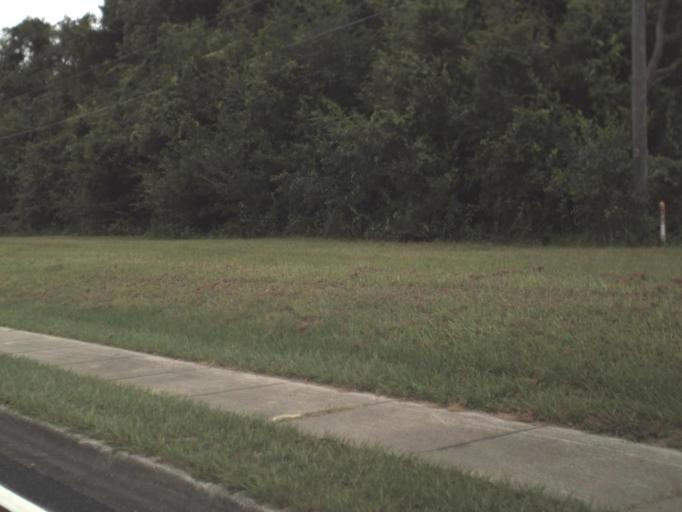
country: US
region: Florida
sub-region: Citrus County
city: Lecanto
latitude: 28.8542
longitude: -82.4984
